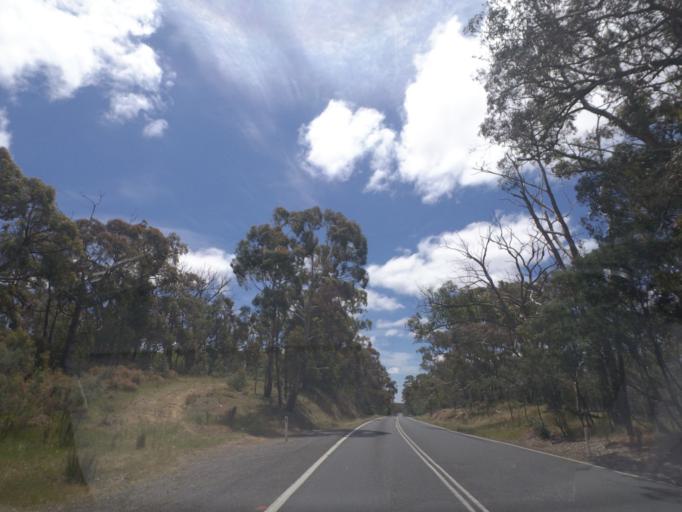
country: AU
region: Victoria
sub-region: Mount Alexander
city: Castlemaine
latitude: -37.2993
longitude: 144.1624
